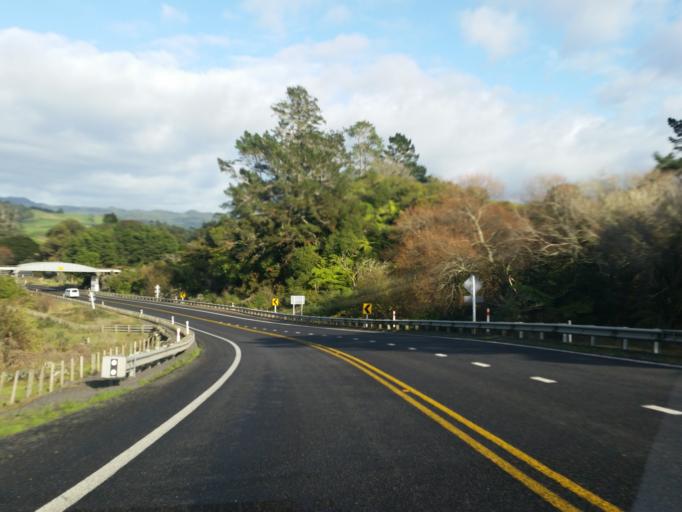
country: NZ
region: Waikato
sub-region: Hauraki District
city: Waihi
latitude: -37.4109
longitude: 175.7985
